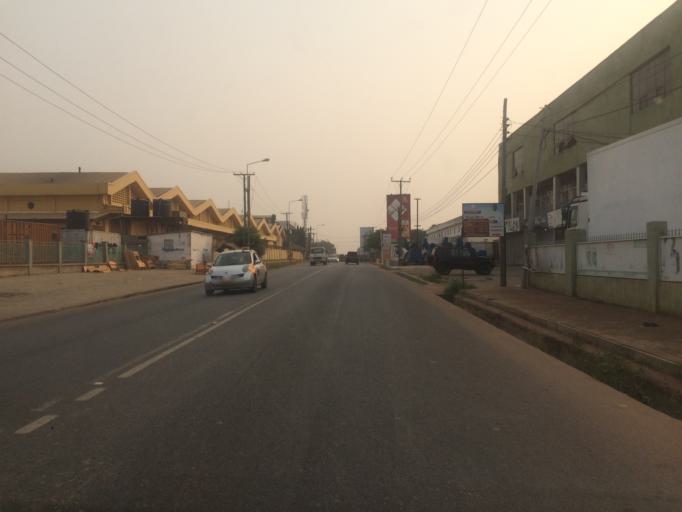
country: GH
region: Greater Accra
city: Medina Estates
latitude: 5.6416
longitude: -0.1167
